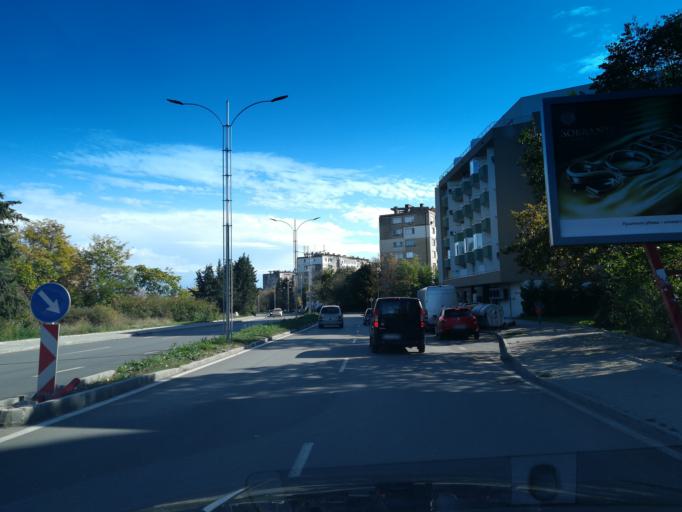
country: BG
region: Stara Zagora
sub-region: Obshtina Stara Zagora
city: Stara Zagora
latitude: 42.4307
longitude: 25.6439
